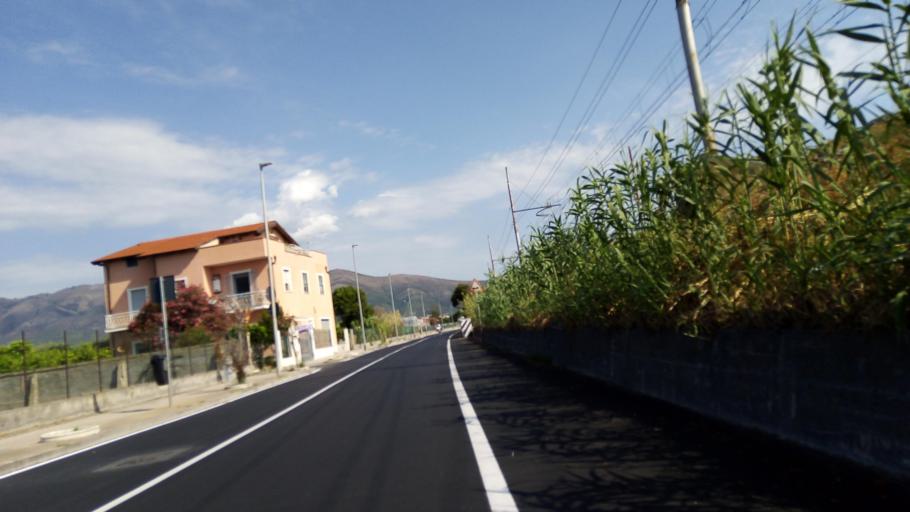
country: IT
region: Liguria
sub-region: Provincia di Savona
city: Albenga
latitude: 44.0644
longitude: 8.2249
